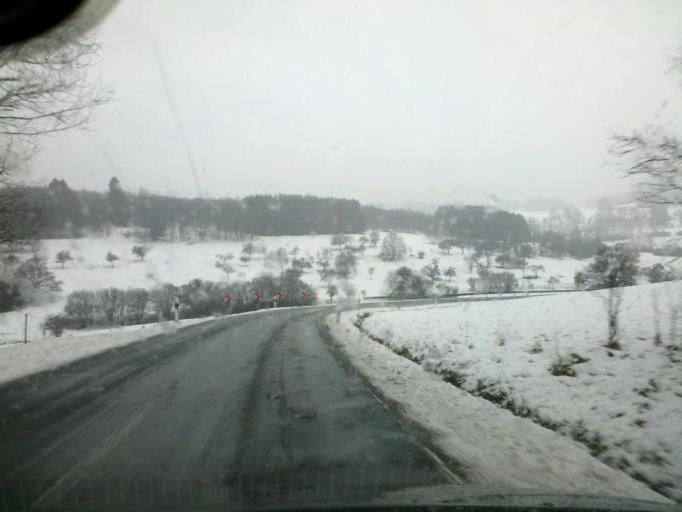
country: DE
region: Hesse
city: Dillenburg
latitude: 50.8108
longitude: 8.2868
